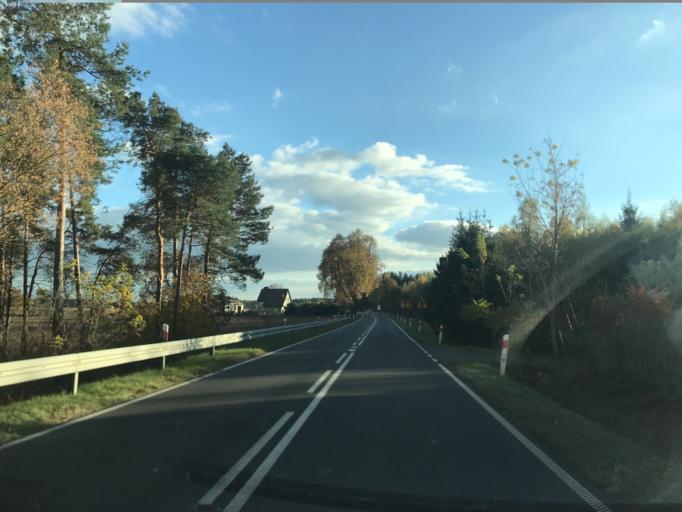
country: PL
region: Warmian-Masurian Voivodeship
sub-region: Powiat dzialdowski
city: Lidzbark
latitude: 53.3080
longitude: 19.8125
